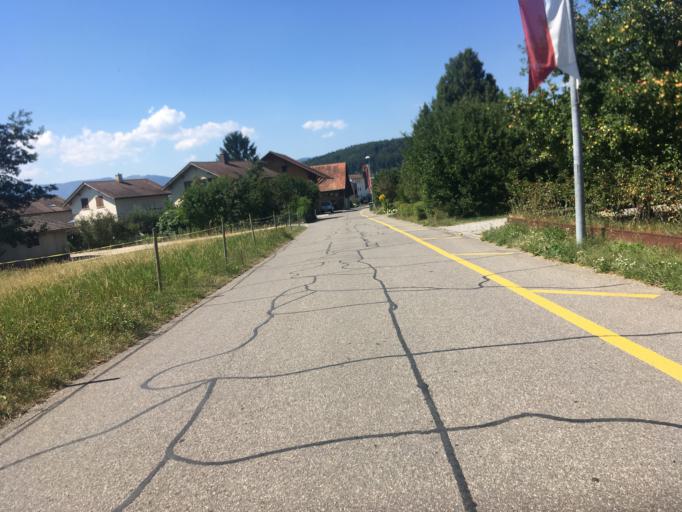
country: CH
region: Bern
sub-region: Seeland District
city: Grossaffoltern
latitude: 47.1102
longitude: 7.3602
